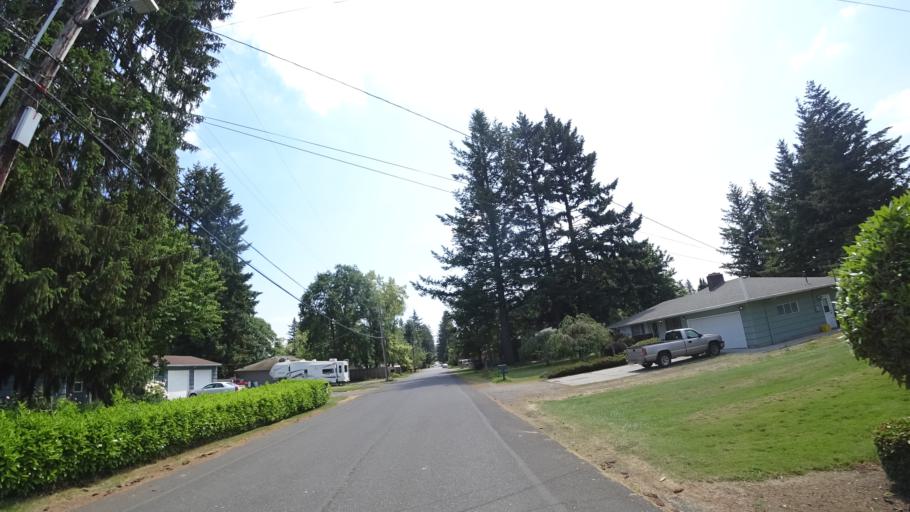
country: US
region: Oregon
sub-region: Multnomah County
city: Lents
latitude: 45.5253
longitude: -122.5081
